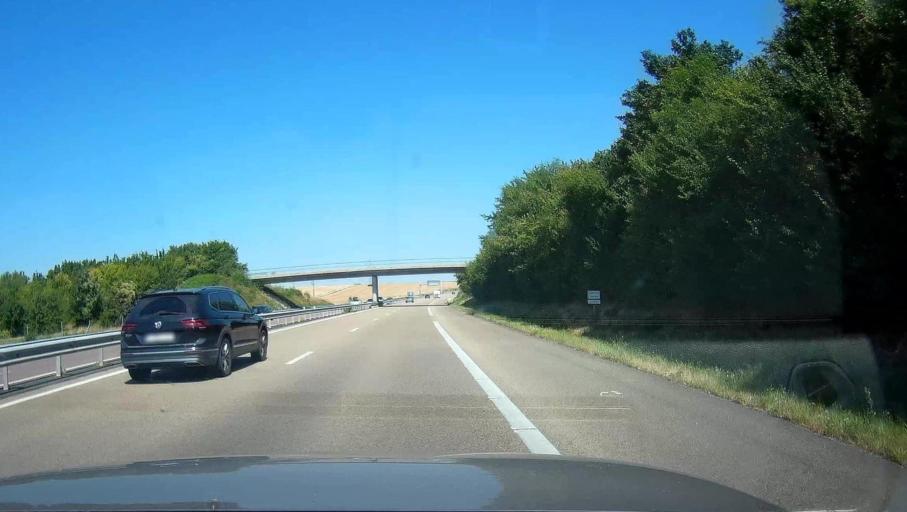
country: FR
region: Champagne-Ardenne
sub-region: Departement de l'Aube
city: Creney-pres-Troyes
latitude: 48.3120
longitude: 4.1642
